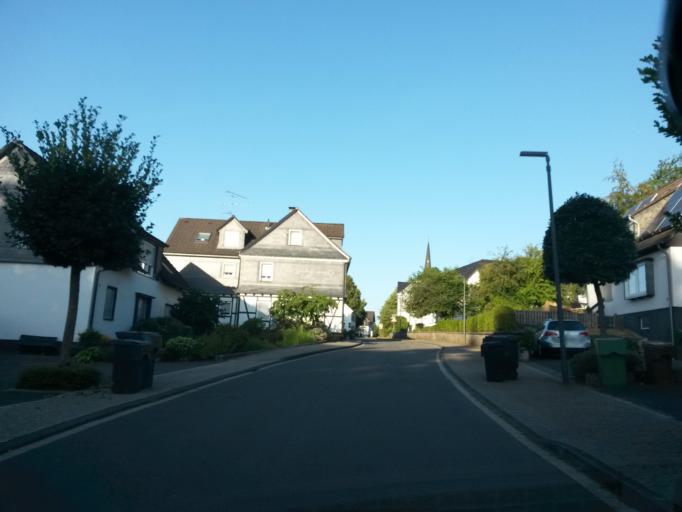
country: DE
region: North Rhine-Westphalia
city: Wipperfurth
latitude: 51.0983
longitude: 7.4246
